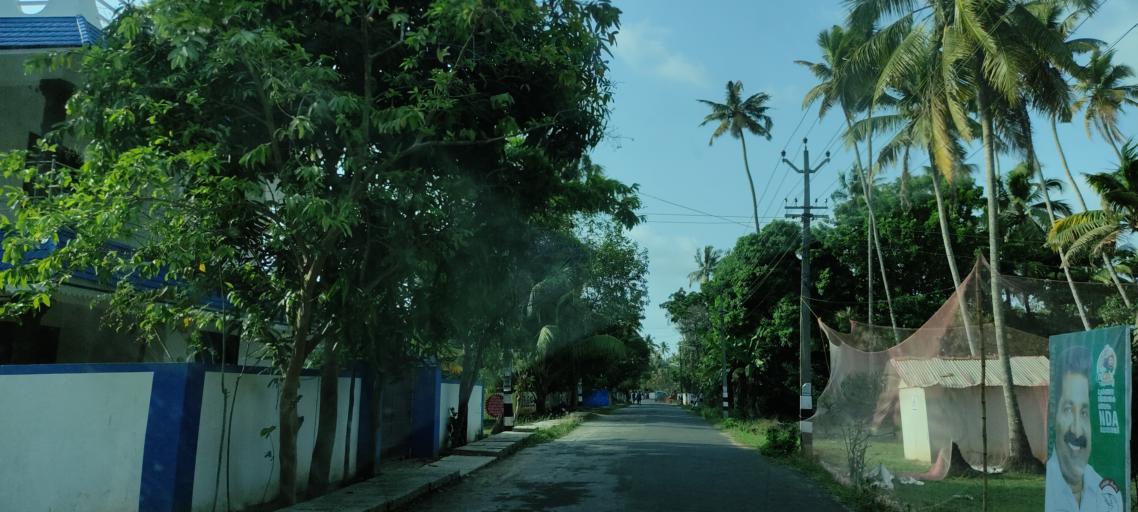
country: IN
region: Kerala
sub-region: Alappuzha
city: Vayalar
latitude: 9.7188
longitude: 76.2876
